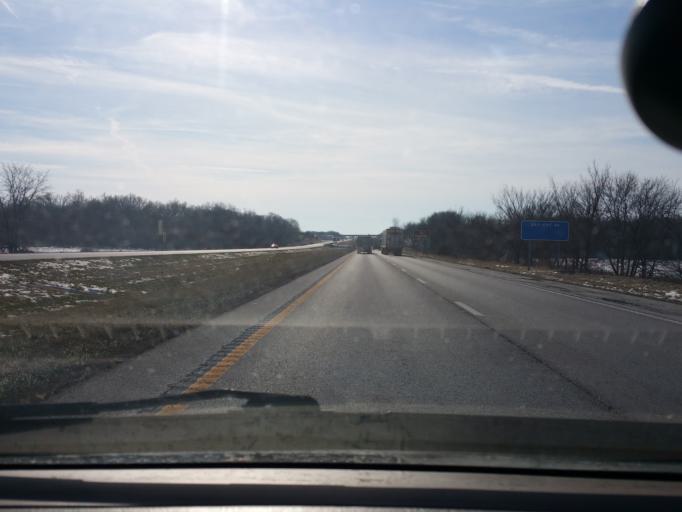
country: US
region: Missouri
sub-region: Clinton County
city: Cameron
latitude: 39.6770
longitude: -94.2335
